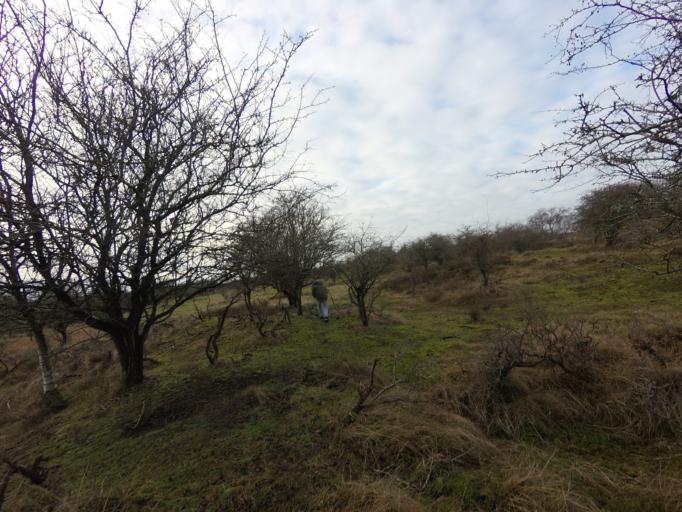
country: NL
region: North Holland
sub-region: Gemeente Zandvoort
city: Zandvoort
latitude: 52.3169
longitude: 4.5289
